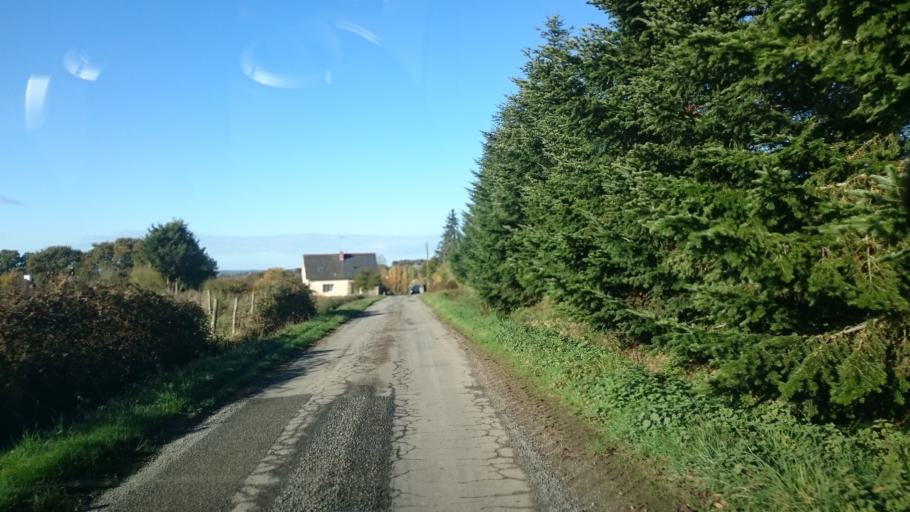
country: FR
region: Brittany
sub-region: Departement d'Ille-et-Vilaine
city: Crevin
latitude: 47.9461
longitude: -1.6804
